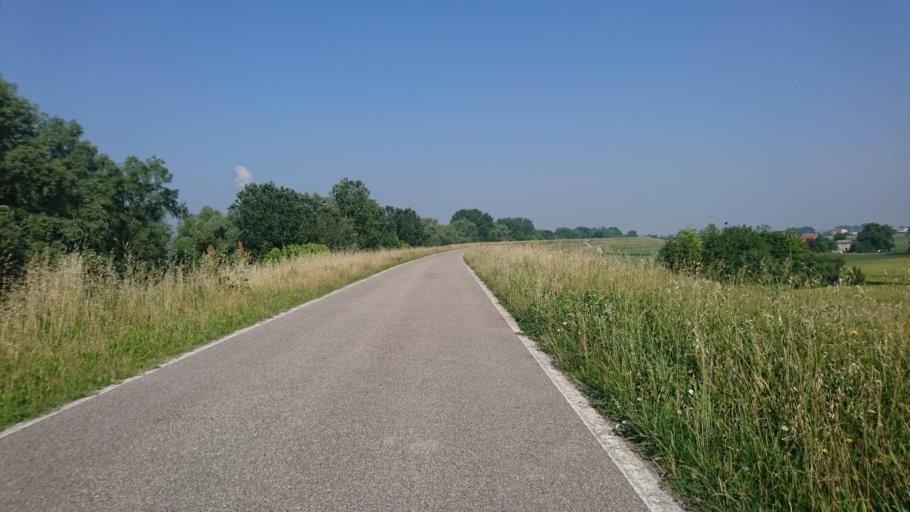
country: IT
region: Lombardy
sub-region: Provincia di Mantova
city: Carbonara di Po
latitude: 45.0507
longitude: 11.2300
